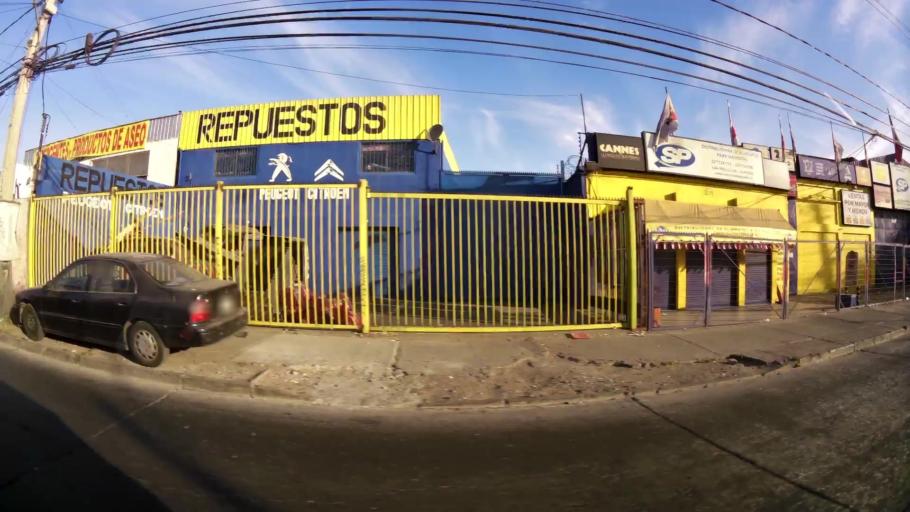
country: CL
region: Santiago Metropolitan
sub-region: Provincia de Santiago
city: Lo Prado
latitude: -33.4419
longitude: -70.7086
